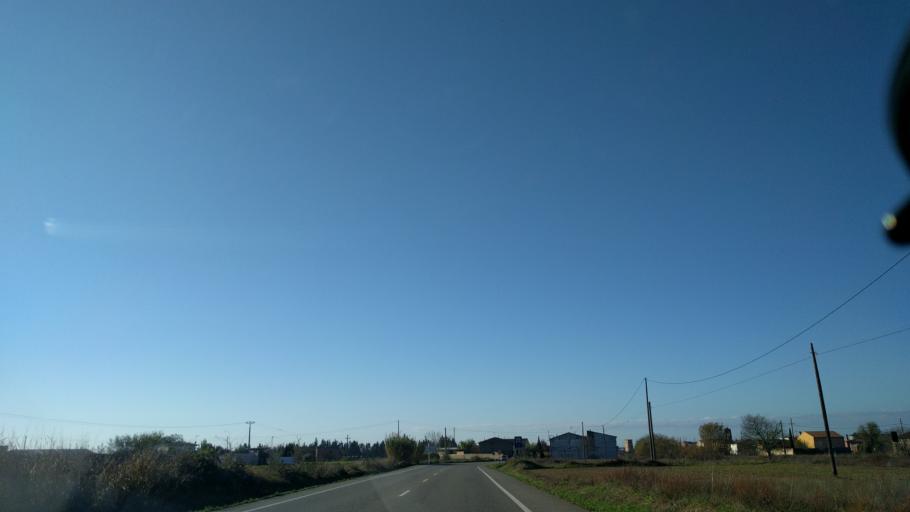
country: ES
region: Catalonia
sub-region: Provincia de Lleida
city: Termens
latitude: 41.7211
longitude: 0.7695
